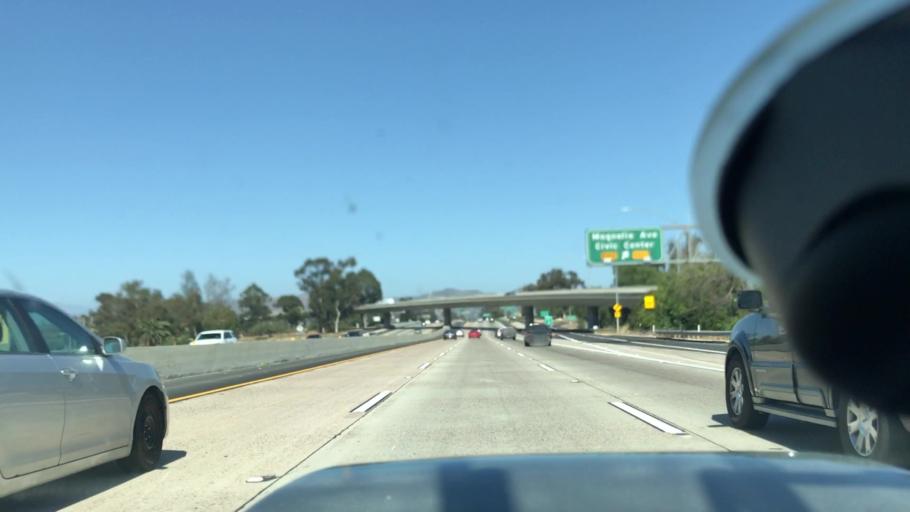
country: US
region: California
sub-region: San Diego County
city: El Cajon
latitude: 32.8032
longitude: -116.9672
